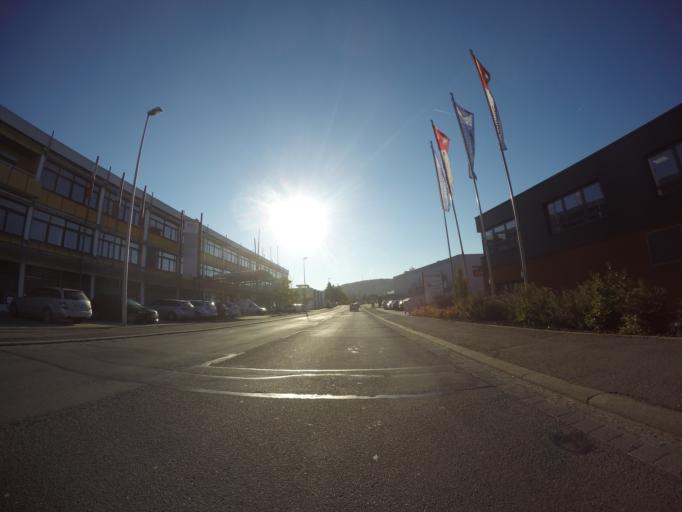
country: DE
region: Bavaria
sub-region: Regierungsbezirk Unterfranken
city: Marktheidenfeld
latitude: 49.8523
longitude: 9.6090
